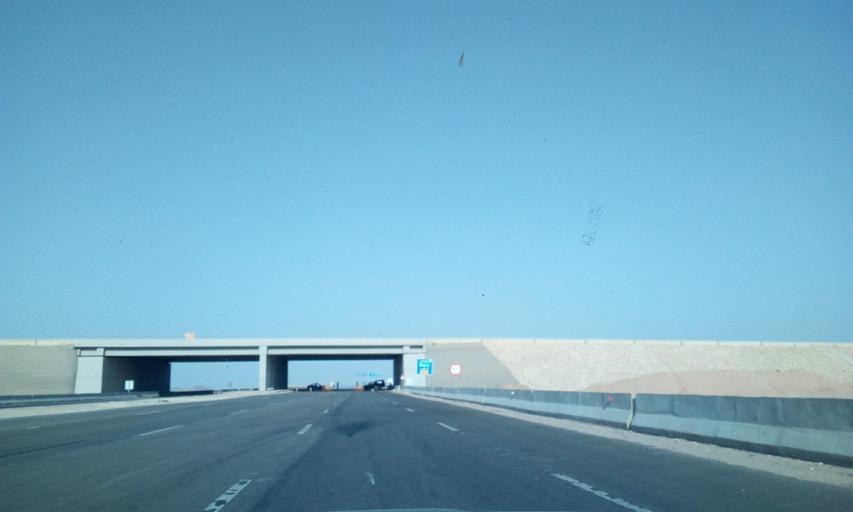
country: EG
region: As Suways
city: Ain Sukhna
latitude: 29.1086
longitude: 32.5319
